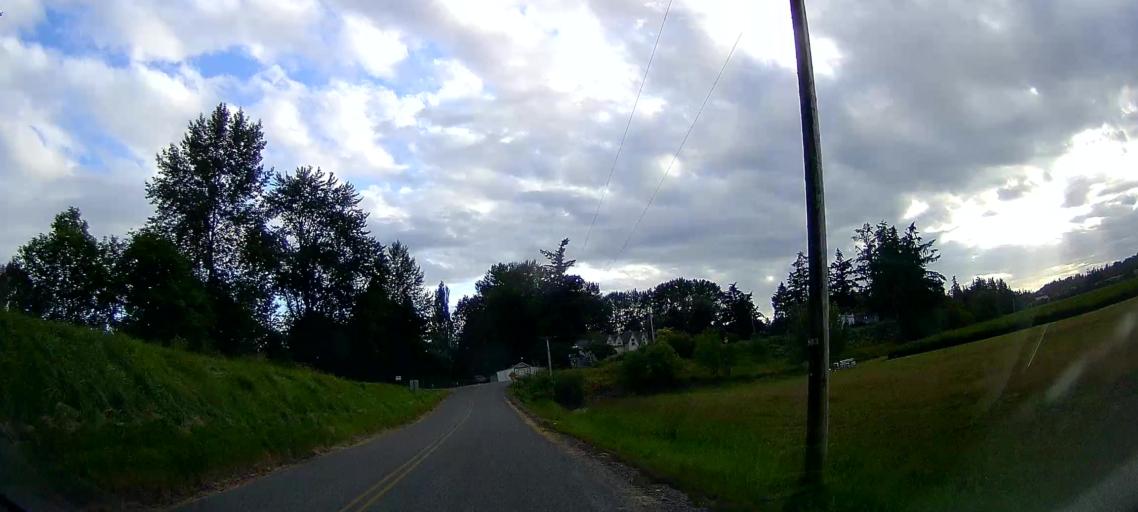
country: US
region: Washington
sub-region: Skagit County
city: Mount Vernon
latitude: 48.3664
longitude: -122.4160
